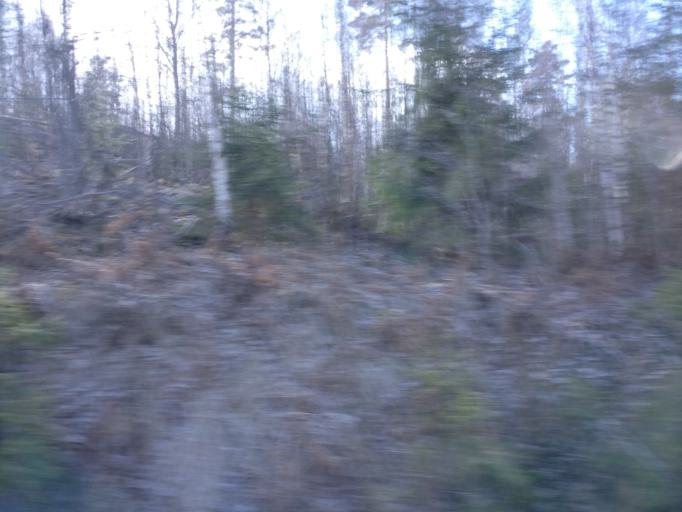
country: FI
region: Varsinais-Suomi
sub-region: Salo
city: Suomusjaervi
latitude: 60.2959
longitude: 23.6401
